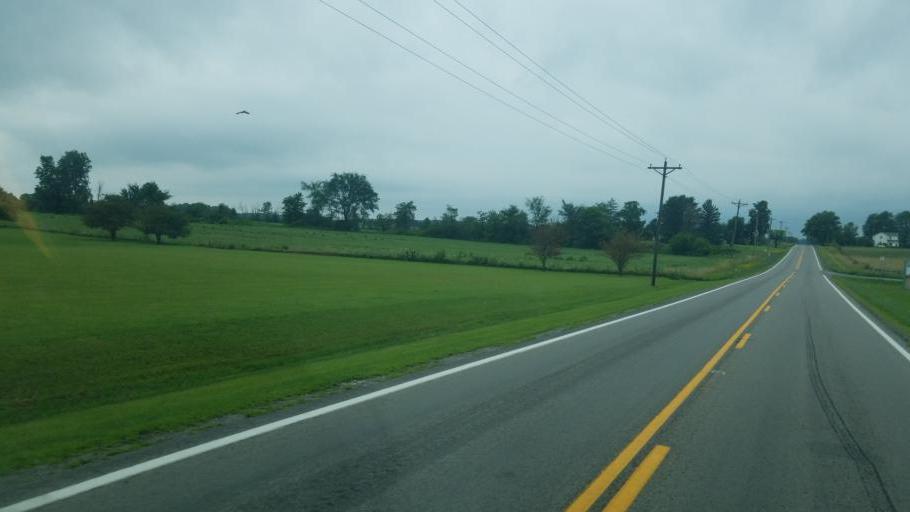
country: US
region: Ohio
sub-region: Logan County
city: Northwood
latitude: 40.5890
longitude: -83.7938
